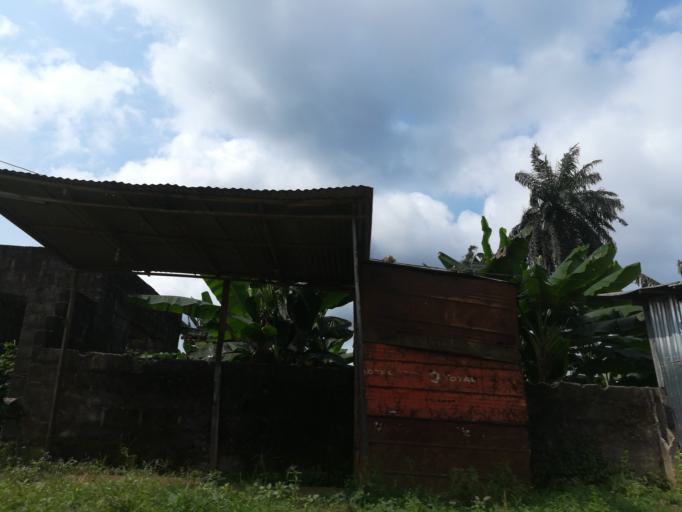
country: NG
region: Rivers
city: Okrika
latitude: 4.7432
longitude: 7.1148
